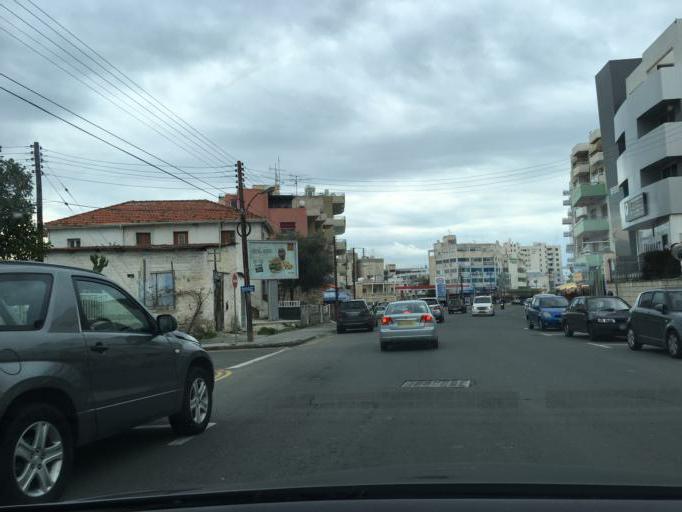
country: CY
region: Limassol
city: Limassol
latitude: 34.6842
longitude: 33.0442
